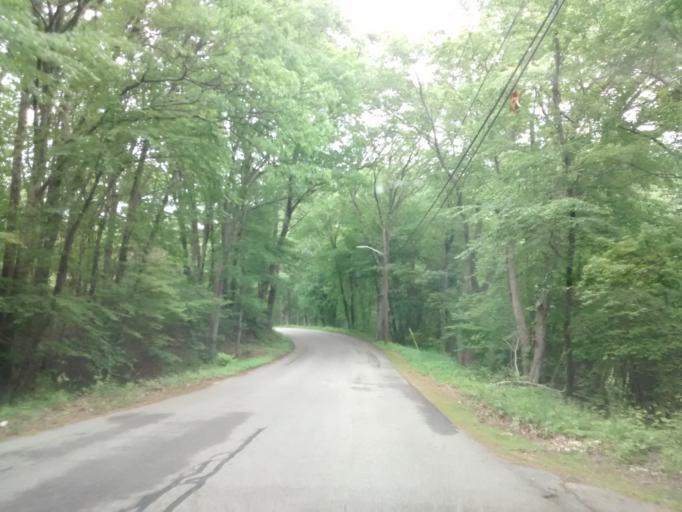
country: US
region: Rhode Island
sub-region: Providence County
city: Harrisville
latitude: 41.9764
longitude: -71.6721
